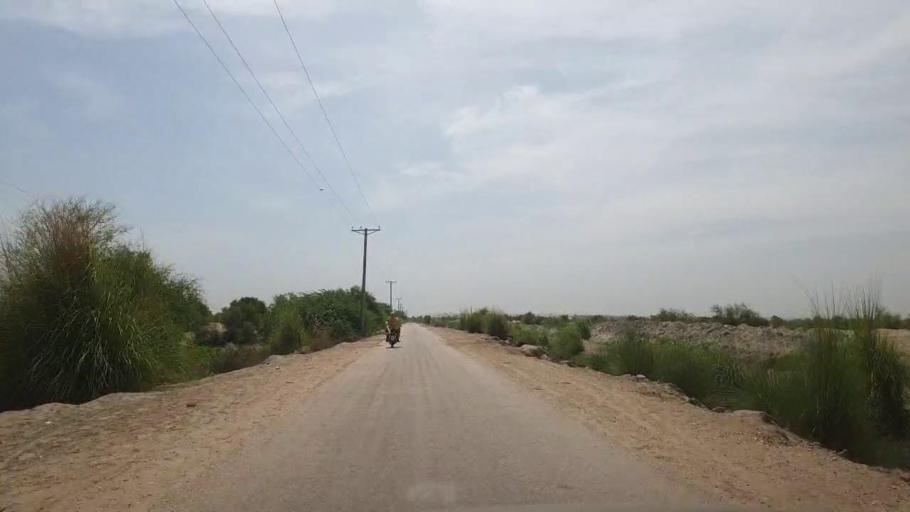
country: PK
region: Sindh
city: Kot Diji
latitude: 27.1164
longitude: 69.0103
